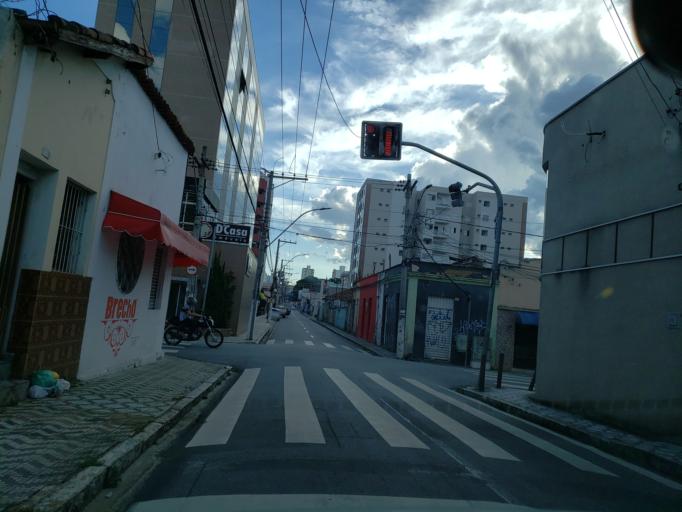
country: BR
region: Sao Paulo
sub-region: Taubate
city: Taubate
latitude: -23.0302
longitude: -45.5584
